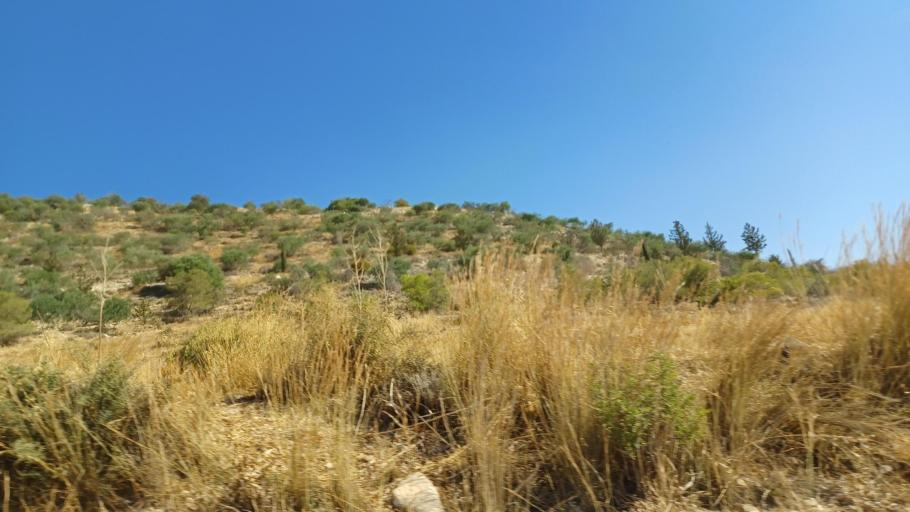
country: CY
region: Lefkosia
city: Lympia
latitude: 34.9779
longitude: 33.5013
